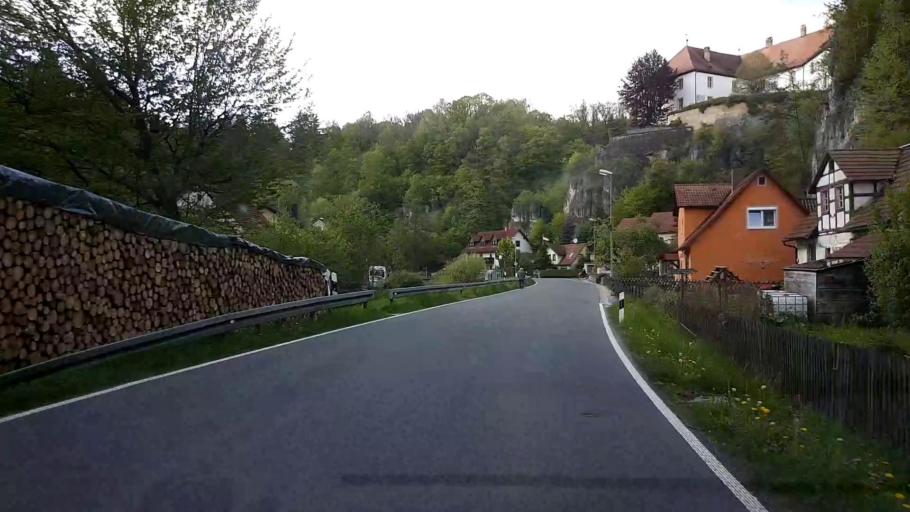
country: DE
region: Bavaria
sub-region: Upper Franconia
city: Hollfeld
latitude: 49.9587
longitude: 11.2555
